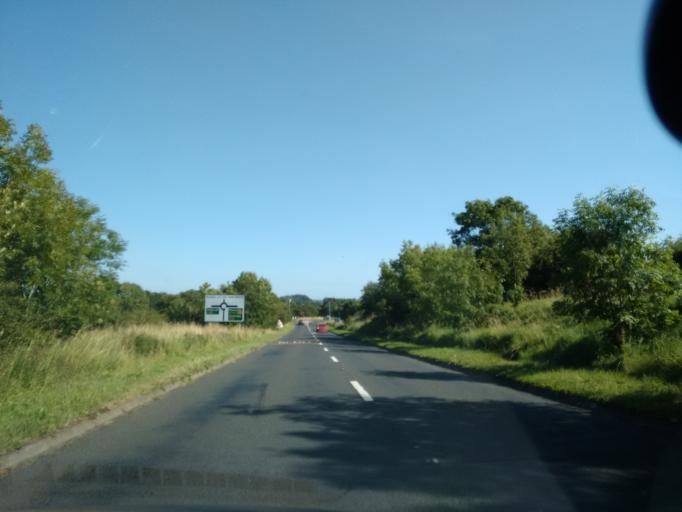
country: GB
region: England
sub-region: Northumberland
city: Corbridge
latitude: 55.0133
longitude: -2.0252
